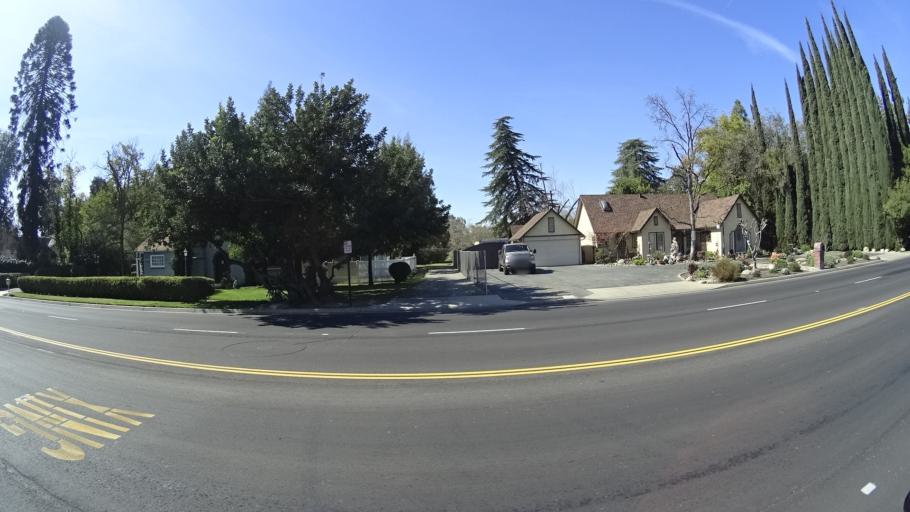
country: US
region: California
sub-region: Fresno County
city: Fresno
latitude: 36.7946
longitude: -119.8086
